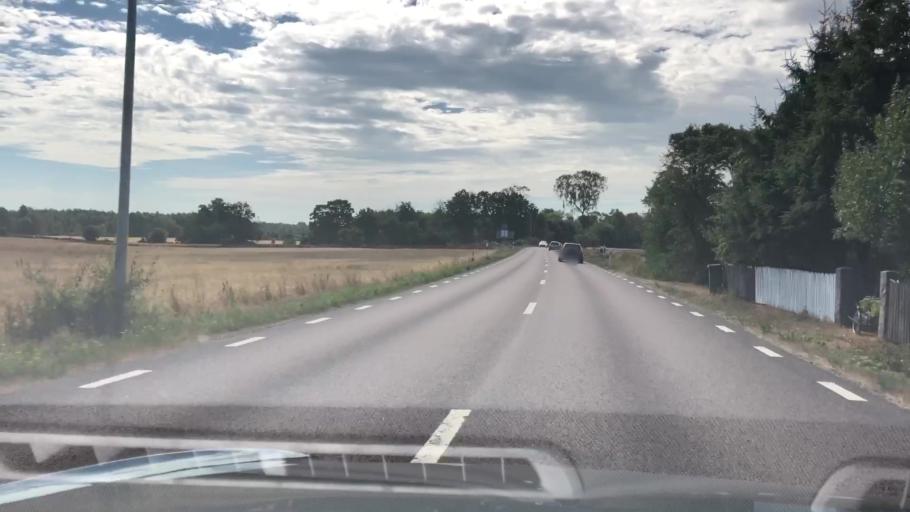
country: SE
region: Kalmar
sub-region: Torsas Kommun
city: Torsas
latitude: 56.3746
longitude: 16.0686
